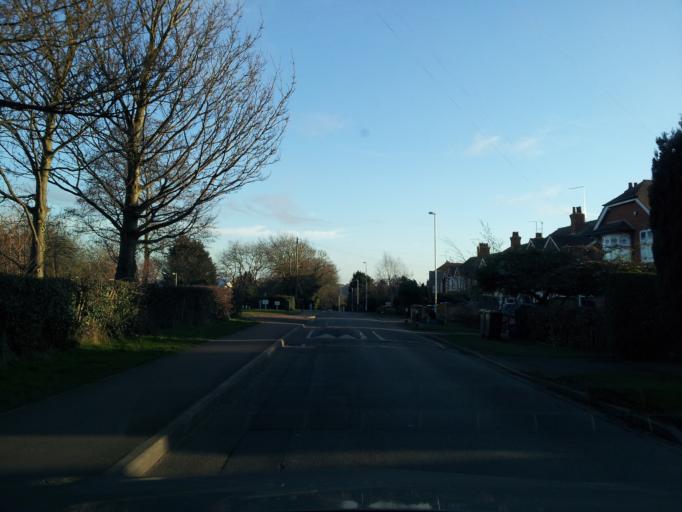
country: GB
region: England
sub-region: Northamptonshire
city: Northampton
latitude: 52.2393
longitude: -0.9410
